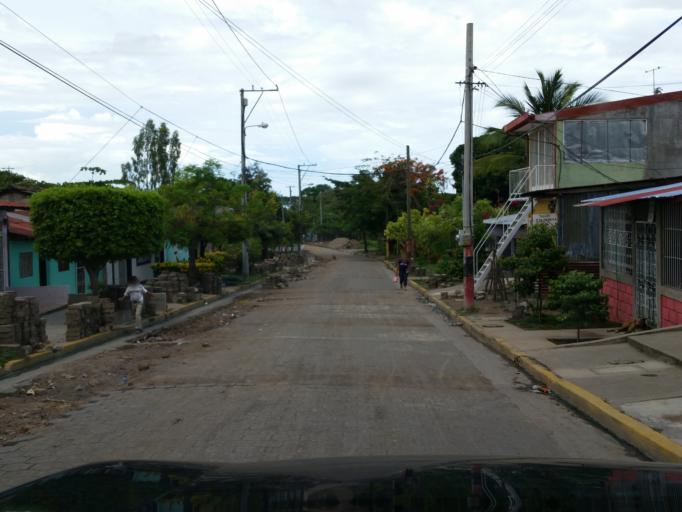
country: NI
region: Granada
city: Granada
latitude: 11.9320
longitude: -85.9474
